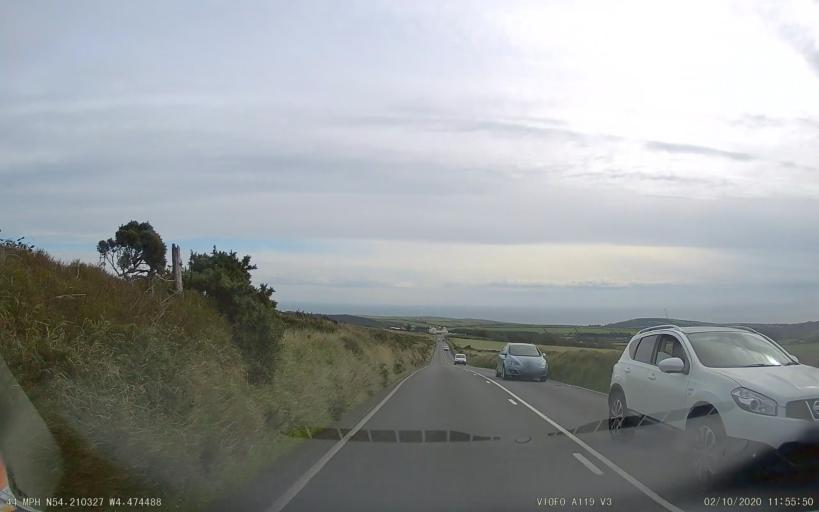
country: IM
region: Douglas
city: Douglas
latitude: 54.2101
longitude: -4.4749
